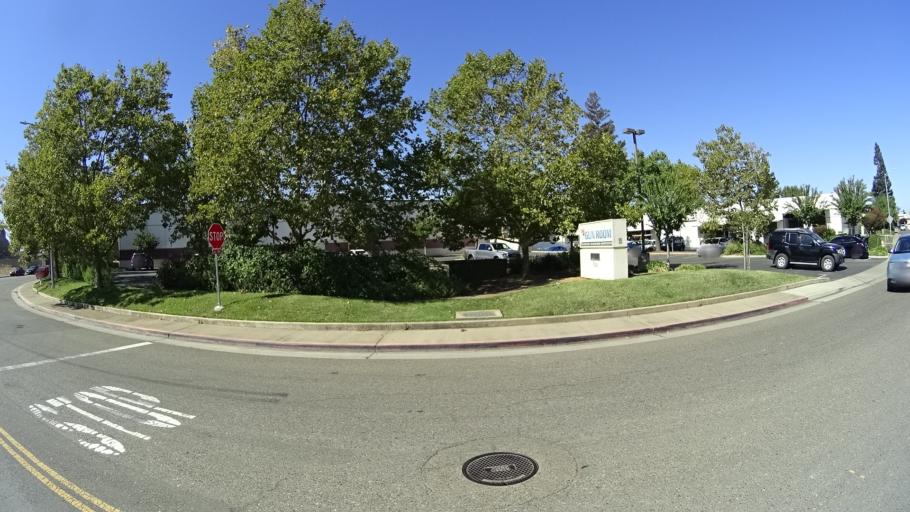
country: US
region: California
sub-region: Sacramento County
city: Elk Grove
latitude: 38.3769
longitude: -121.3569
